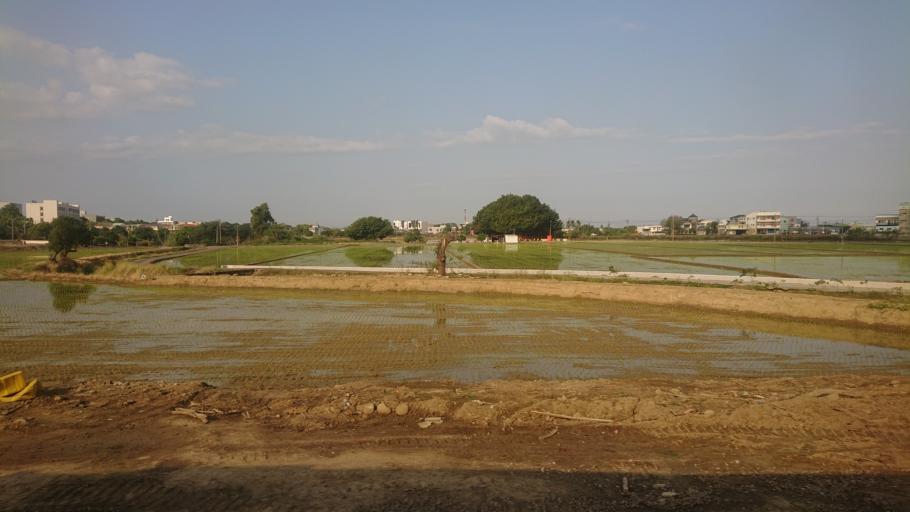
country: TW
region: Taiwan
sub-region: Chiayi
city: Jiayi Shi
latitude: 23.5467
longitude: 120.4292
